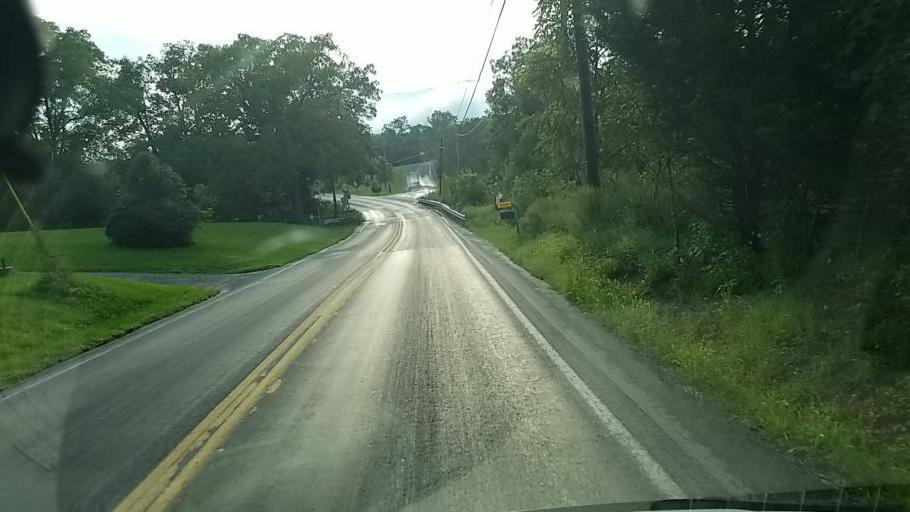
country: US
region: Pennsylvania
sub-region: Cumberland County
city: Newville
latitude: 40.1886
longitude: -77.5259
